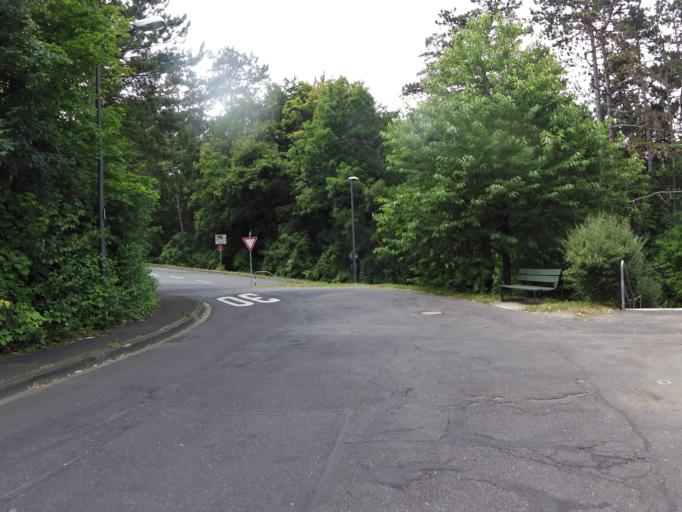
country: DE
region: Bavaria
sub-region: Regierungsbezirk Unterfranken
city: Wuerzburg
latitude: 49.7718
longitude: 9.9246
